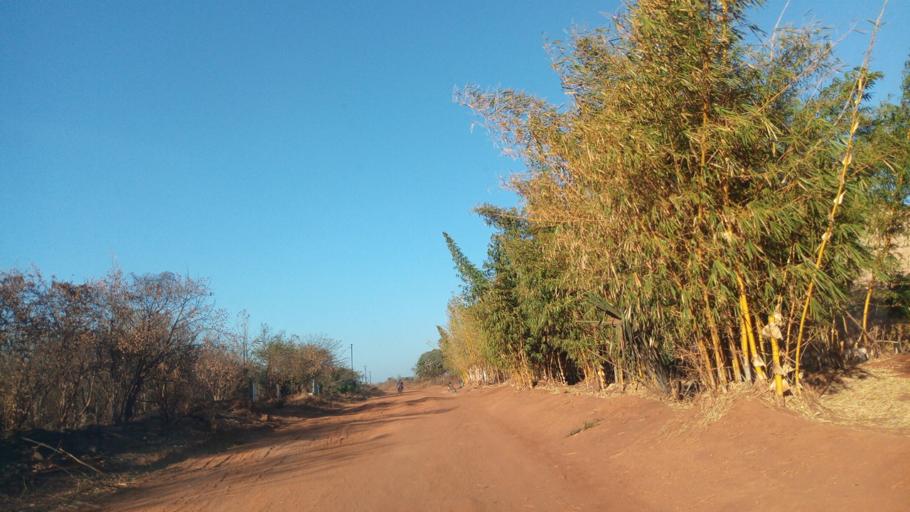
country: ZM
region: Luapula
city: Mwense
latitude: -10.4108
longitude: 28.6105
